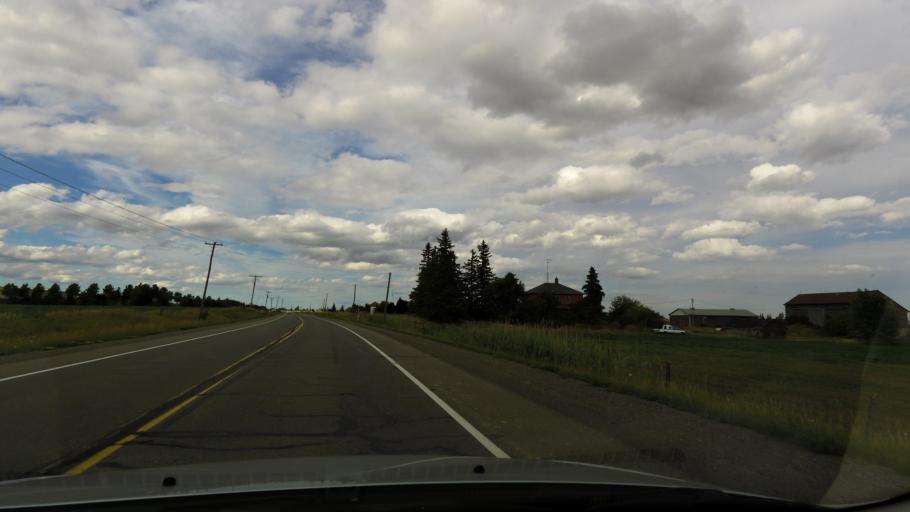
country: CA
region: Ontario
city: Brampton
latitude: 43.6880
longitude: -79.8735
